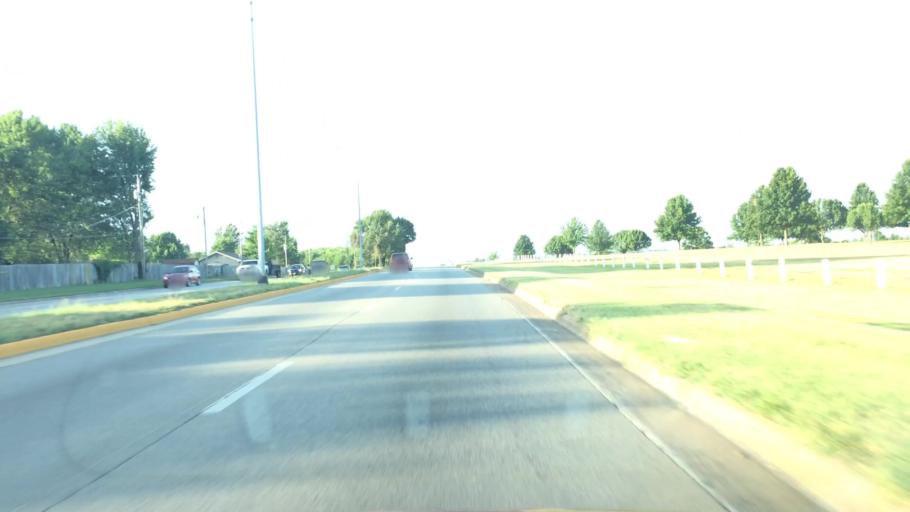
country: US
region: Missouri
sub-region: Greene County
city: Springfield
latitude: 37.1787
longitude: -93.3182
